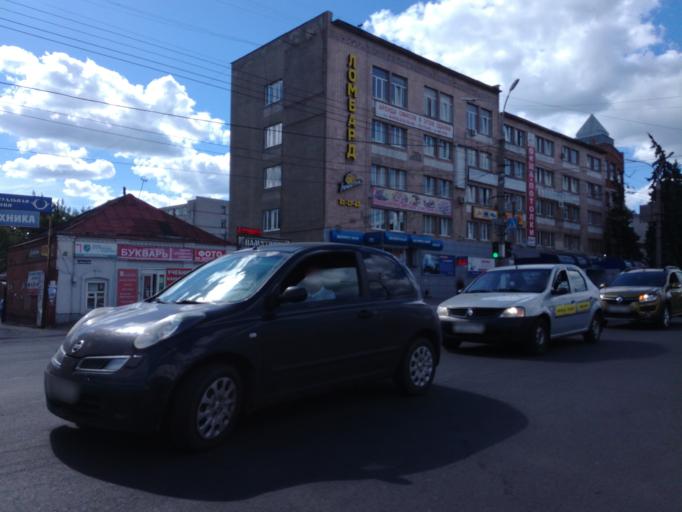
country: RU
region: Kursk
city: Kursk
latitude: 51.7575
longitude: 36.1879
